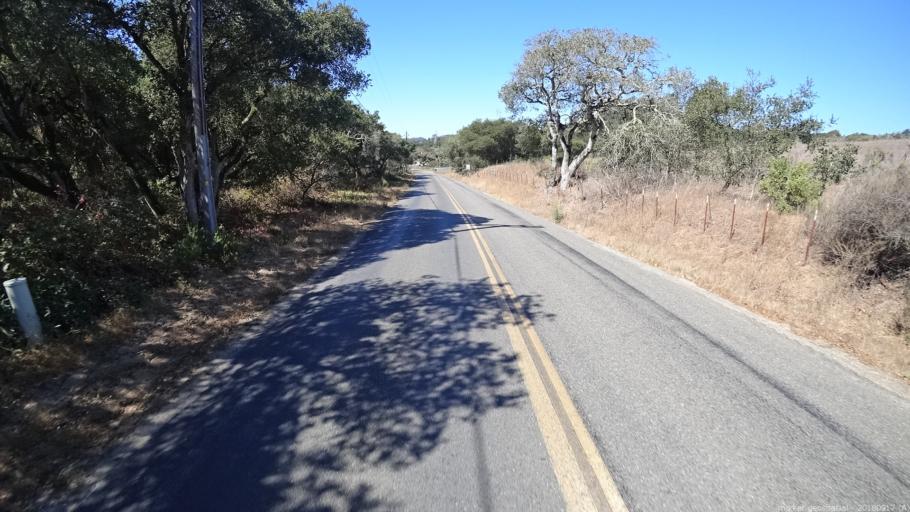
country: US
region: California
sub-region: Monterey County
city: Elkhorn
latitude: 36.8324
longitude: -121.6934
